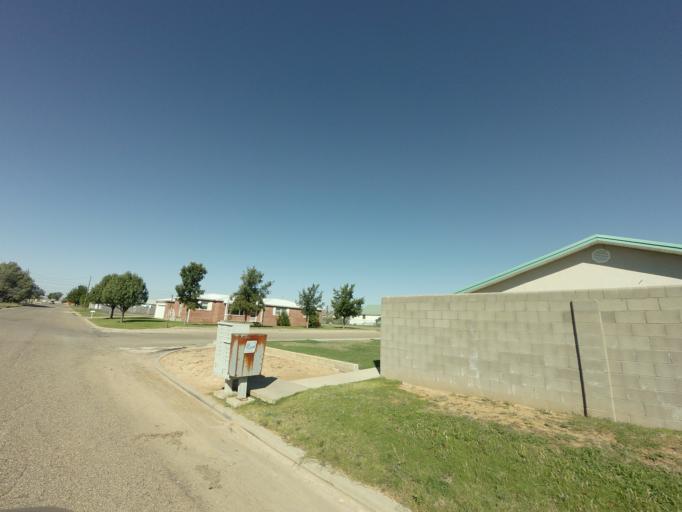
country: US
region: New Mexico
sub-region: Curry County
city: Clovis
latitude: 34.4320
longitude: -103.1938
